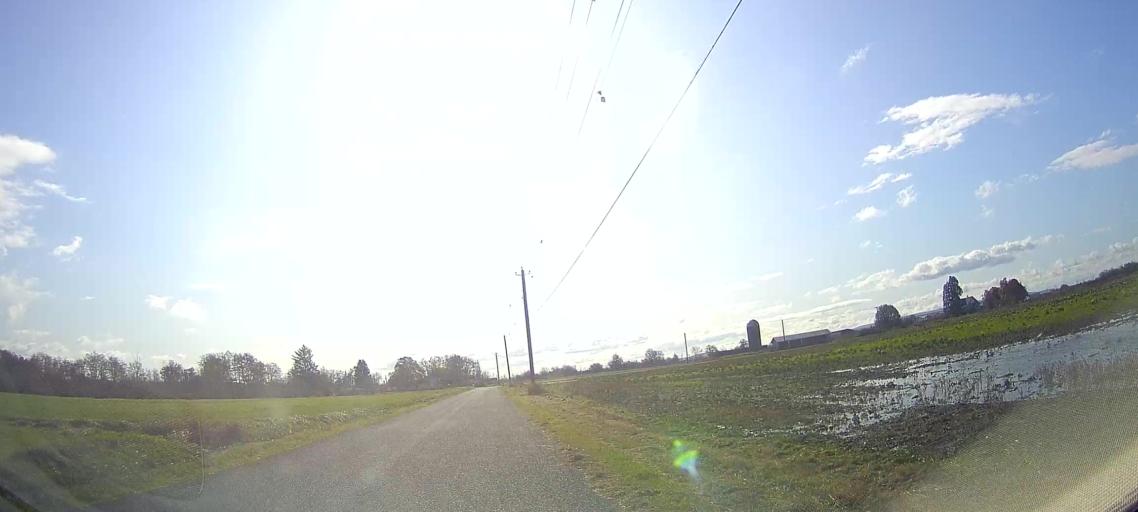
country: US
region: Washington
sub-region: Snohomish County
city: Stanwood
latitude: 48.3289
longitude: -122.3790
